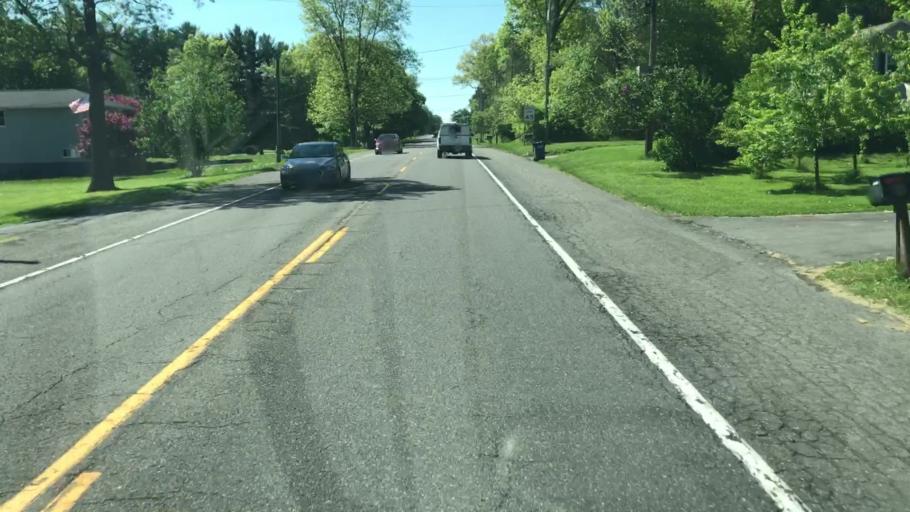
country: US
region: New York
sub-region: Onondaga County
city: Seneca Knolls
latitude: 43.1332
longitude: -76.2575
